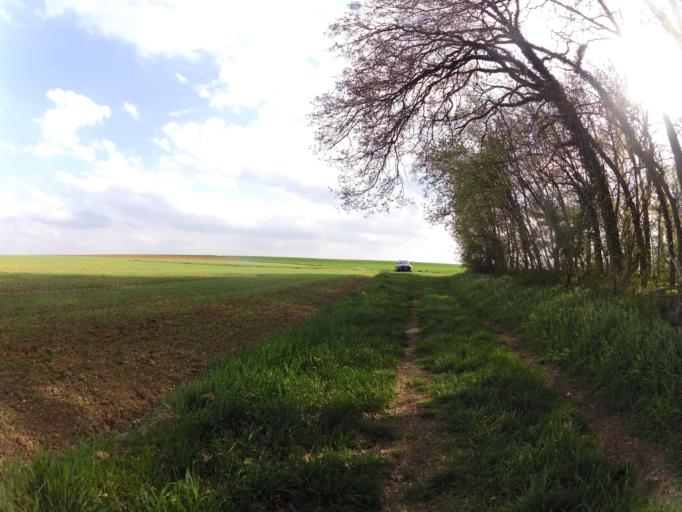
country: DE
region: Bavaria
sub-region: Regierungsbezirk Unterfranken
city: Winterhausen
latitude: 49.6927
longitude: 10.0043
